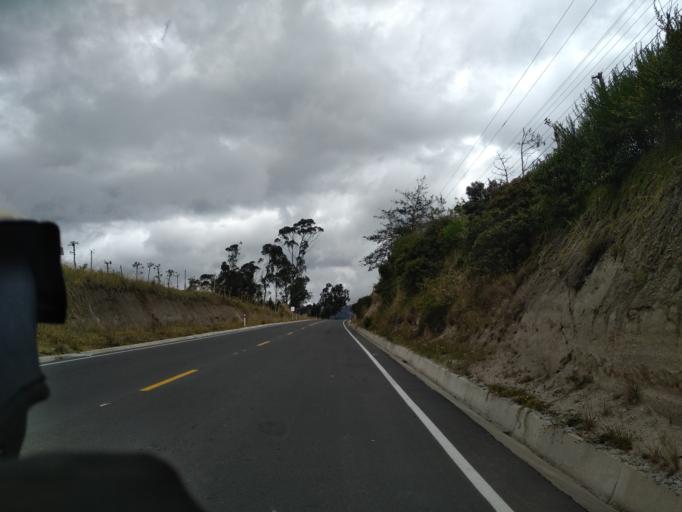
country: EC
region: Cotopaxi
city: Saquisili
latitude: -0.7909
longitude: -78.9127
